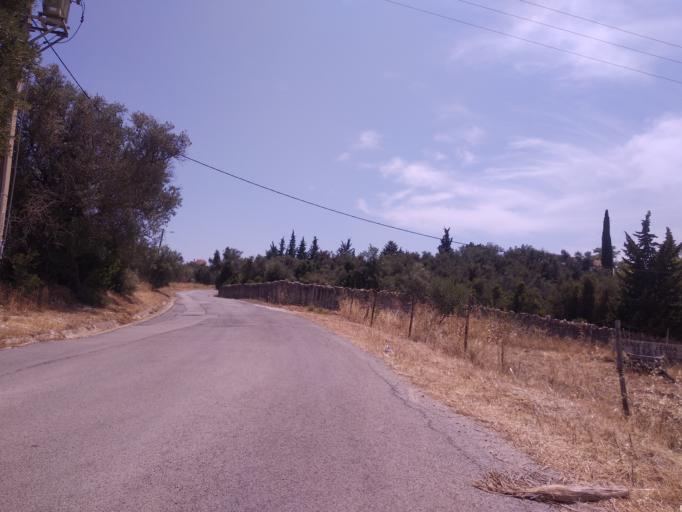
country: PT
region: Faro
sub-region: Faro
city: Santa Barbara de Nexe
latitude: 37.1235
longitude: -7.9394
